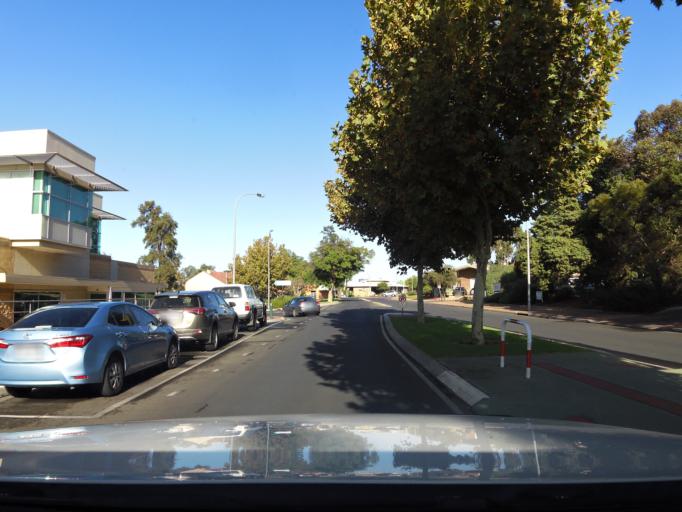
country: AU
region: South Australia
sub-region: Berri and Barmera
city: Berri
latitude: -34.2846
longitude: 140.6031
